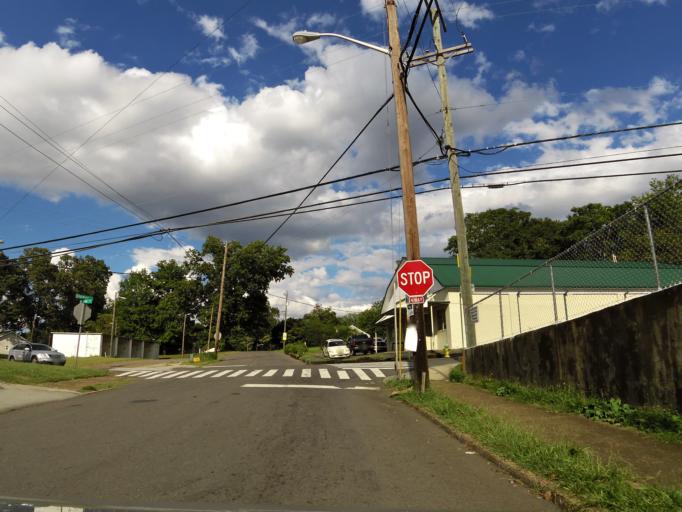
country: US
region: Tennessee
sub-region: Knox County
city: Knoxville
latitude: 36.0044
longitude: -83.9132
